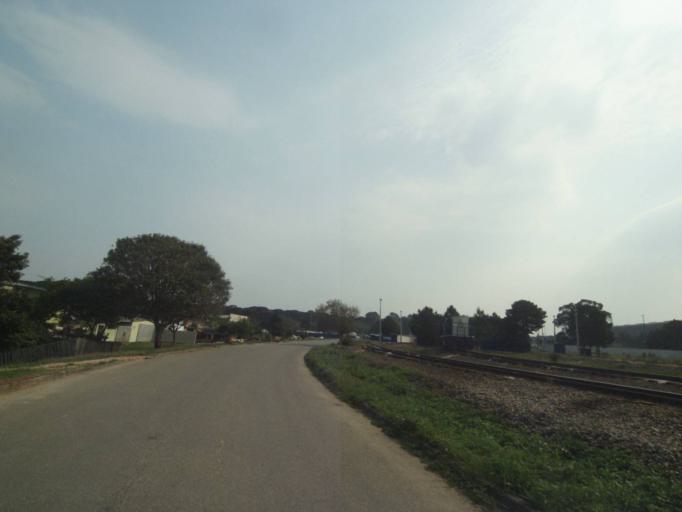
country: BR
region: Parana
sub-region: Sao Jose Dos Pinhais
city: Sao Jose dos Pinhais
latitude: -25.5395
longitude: -49.2343
